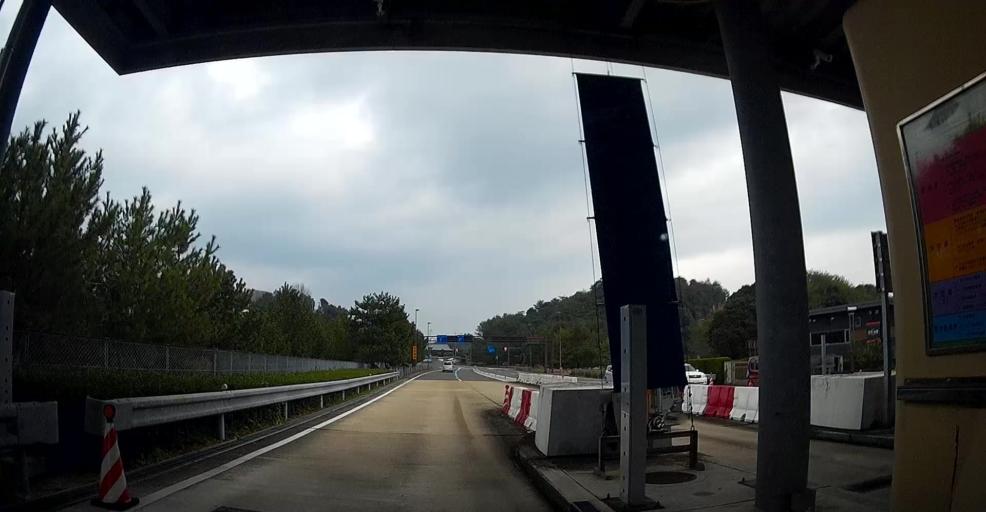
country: JP
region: Kumamoto
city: Yatsushiro
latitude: 32.5209
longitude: 130.4189
